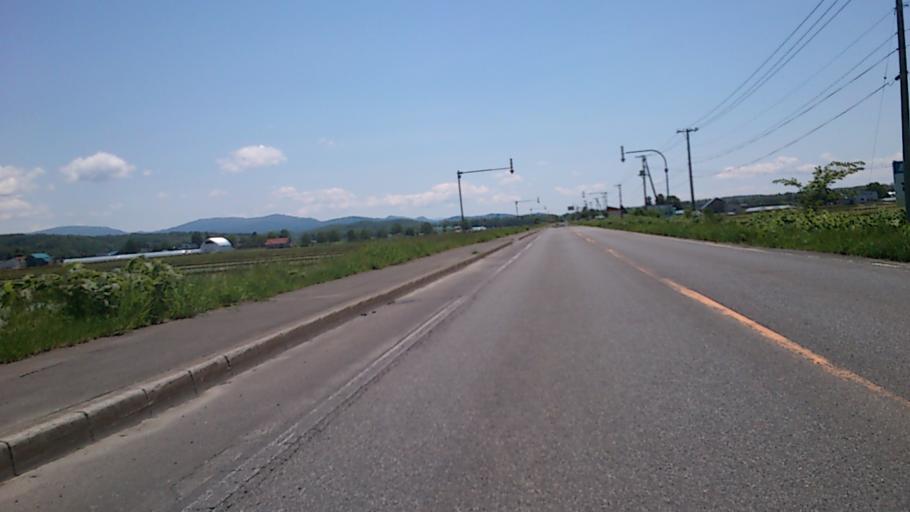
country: JP
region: Hokkaido
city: Nayoro
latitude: 44.3214
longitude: 142.4577
